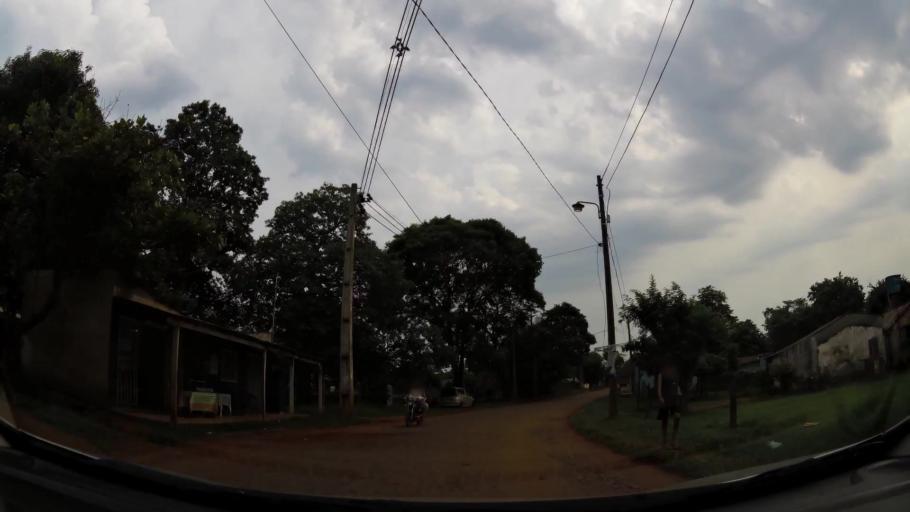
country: PY
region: Alto Parana
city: Presidente Franco
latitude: -25.5490
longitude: -54.6448
